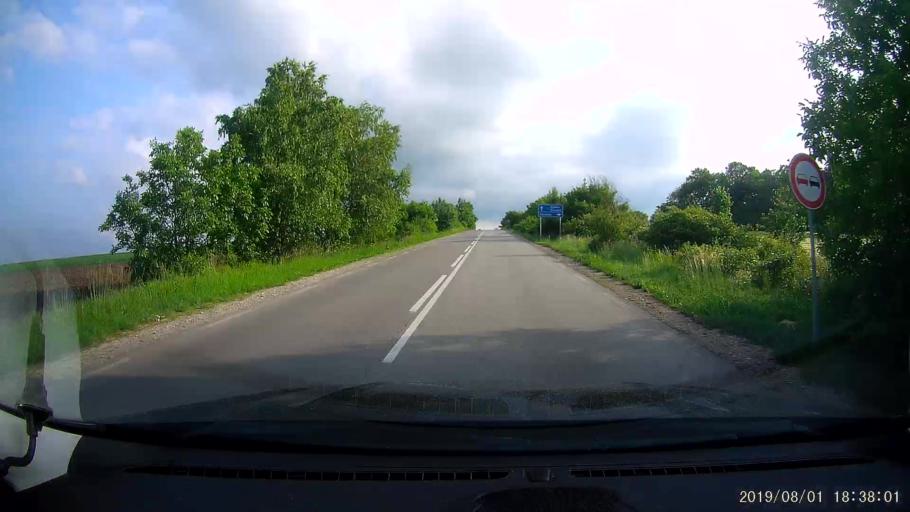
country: BG
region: Shumen
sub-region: Obshtina Khitrino
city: Gara Khitrino
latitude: 43.4091
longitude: 26.9220
